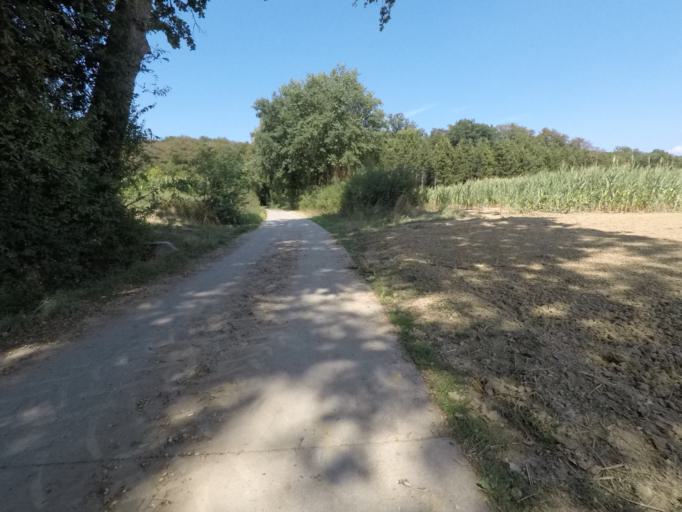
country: LU
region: Luxembourg
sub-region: Canton de Capellen
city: Garnich
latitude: 49.6299
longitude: 5.9471
